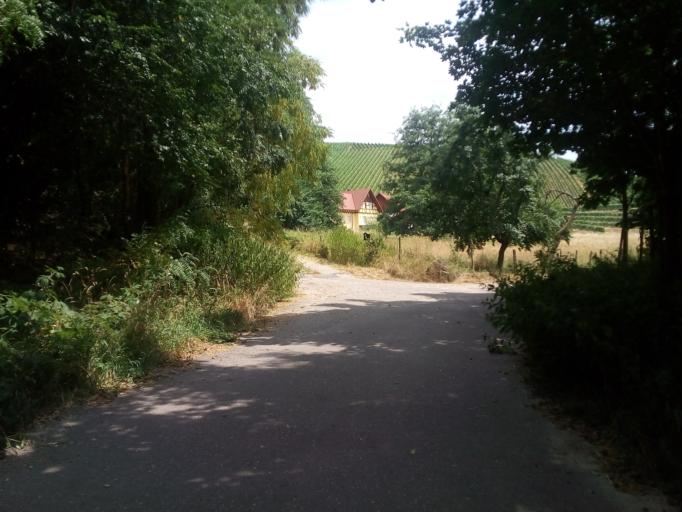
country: DE
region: Baden-Wuerttemberg
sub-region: Freiburg Region
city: Achern
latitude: 48.6081
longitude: 8.0894
